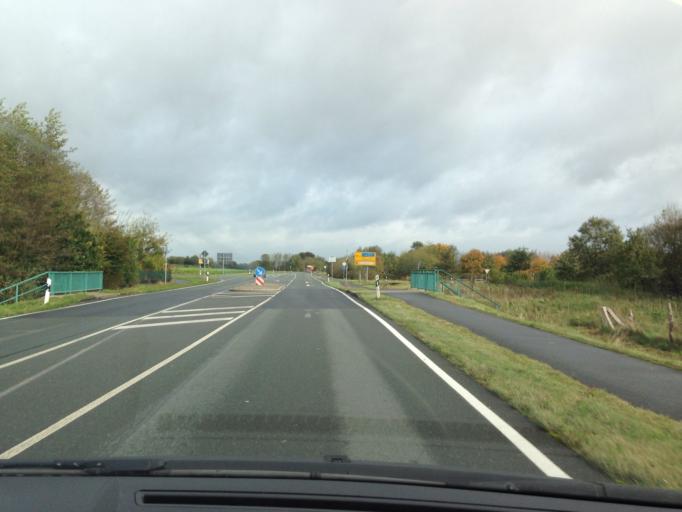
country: DE
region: North Rhine-Westphalia
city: Ludinghausen
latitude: 51.7723
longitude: 7.4713
